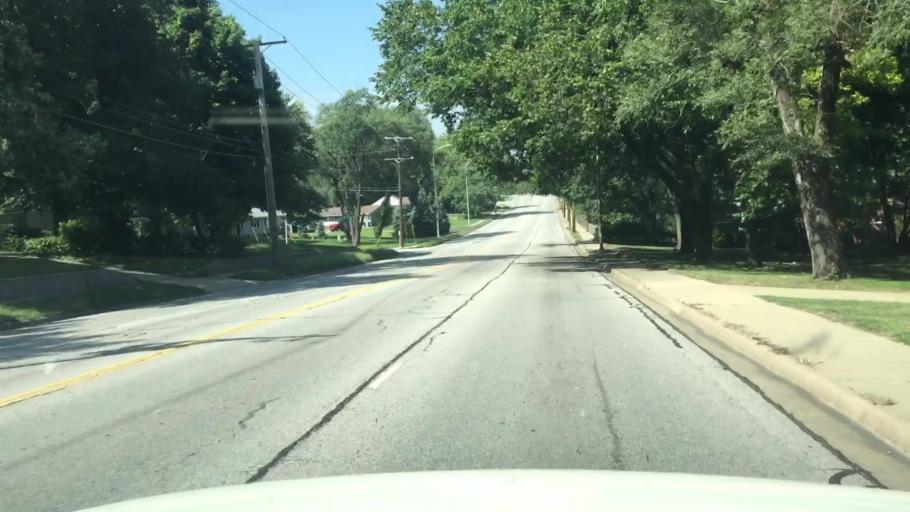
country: US
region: Kansas
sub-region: Johnson County
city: Overland Park
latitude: 38.9742
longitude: -94.6676
